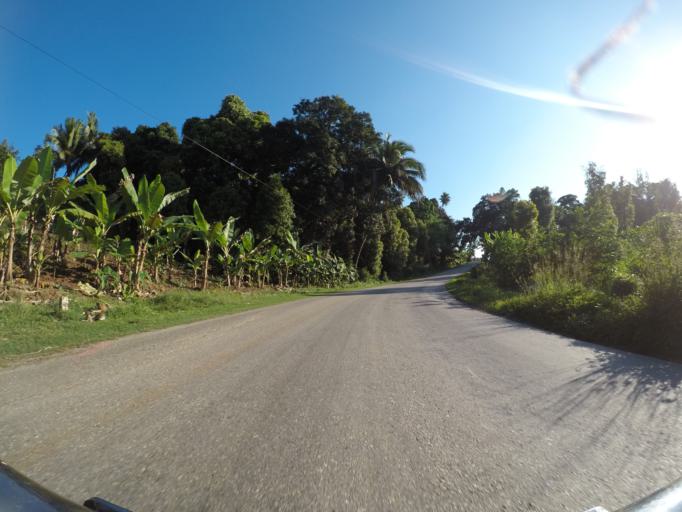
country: TZ
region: Pemba South
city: Mtambile
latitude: -5.3743
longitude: 39.7053
